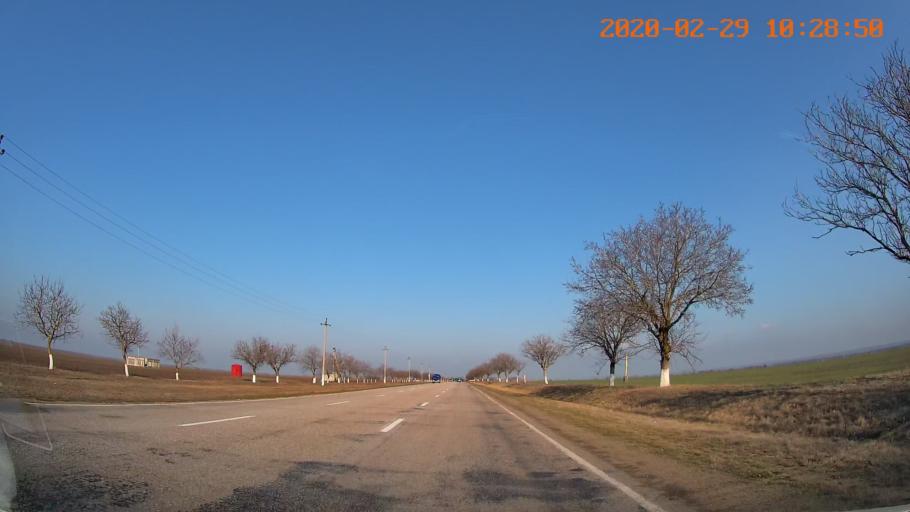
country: MD
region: Telenesti
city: Tiraspolul Nou
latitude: 46.9160
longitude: 29.5891
